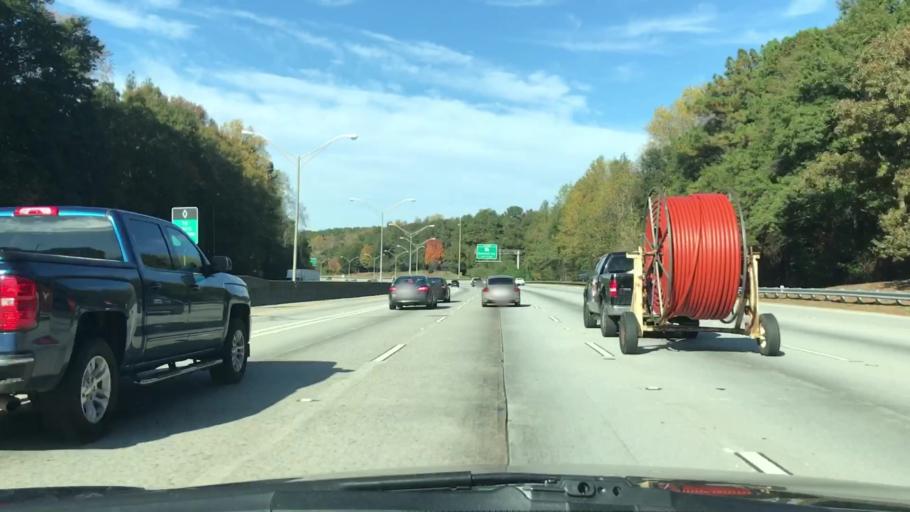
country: US
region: Georgia
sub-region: DeKalb County
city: Gresham Park
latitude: 33.7303
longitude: -84.3229
